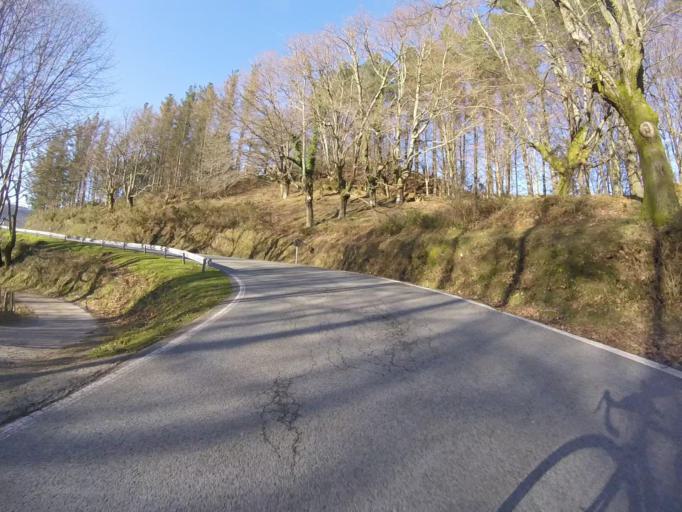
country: ES
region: Navarre
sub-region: Provincia de Navarra
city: Lesaka
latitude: 43.2603
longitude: -1.7358
